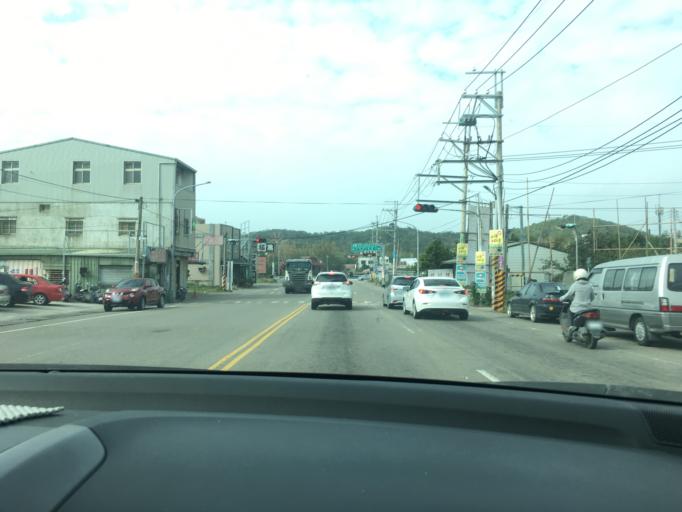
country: TW
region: Taiwan
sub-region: Miaoli
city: Miaoli
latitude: 24.4970
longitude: 120.6944
